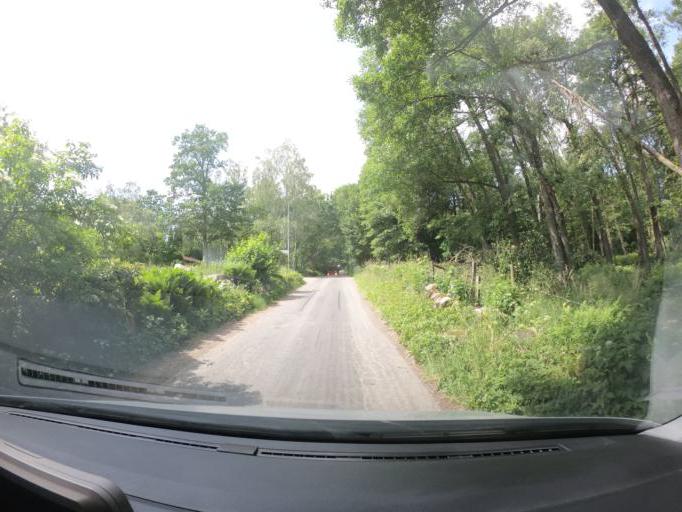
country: SE
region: Skane
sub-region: Hassleholms Kommun
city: Sosdala
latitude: 55.9889
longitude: 13.6315
